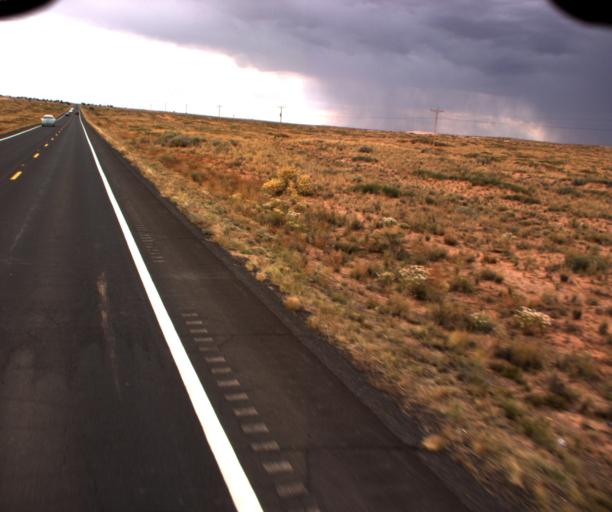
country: US
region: Arizona
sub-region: Coconino County
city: Tuba City
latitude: 36.2579
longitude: -111.0198
